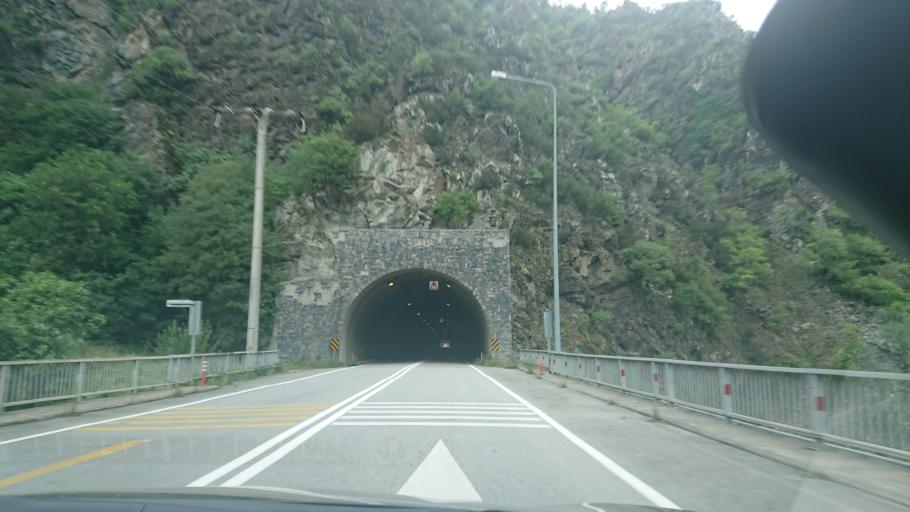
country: TR
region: Gumushane
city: Kurtun
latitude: 40.7347
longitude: 39.0021
